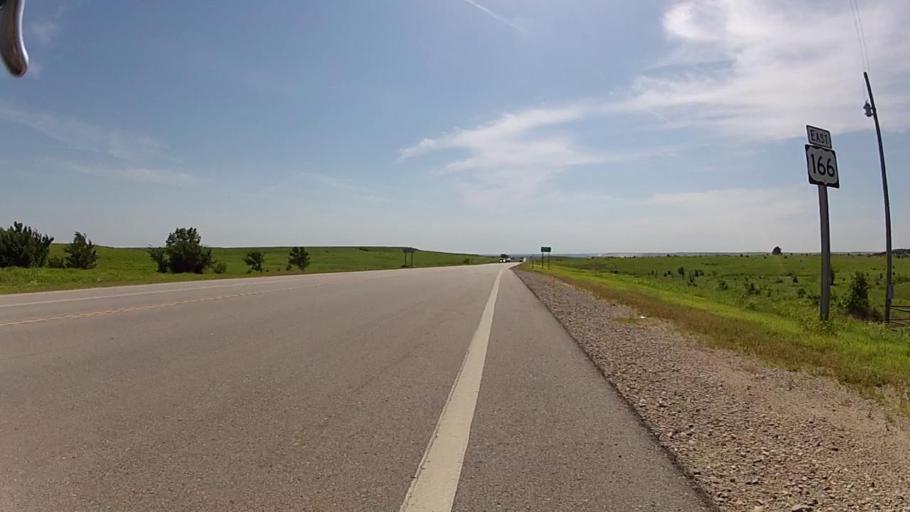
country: US
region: Kansas
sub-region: Cowley County
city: Winfield
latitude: 37.1106
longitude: -96.6428
